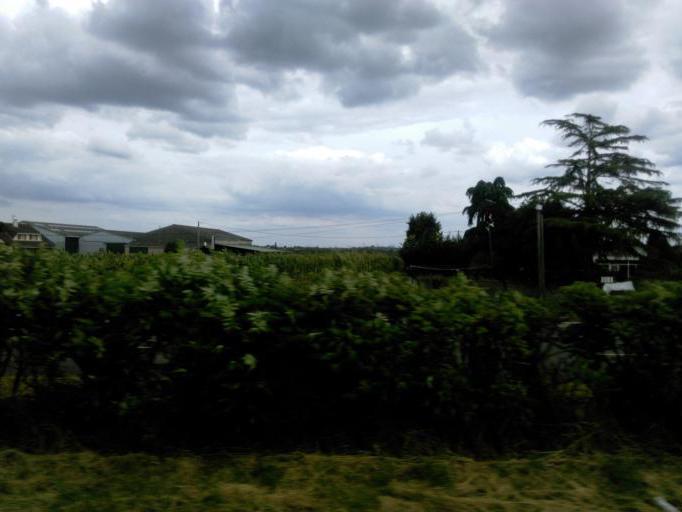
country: FR
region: Ile-de-France
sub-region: Departement du Val-d'Oise
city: Osny
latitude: 49.0779
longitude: 2.0735
